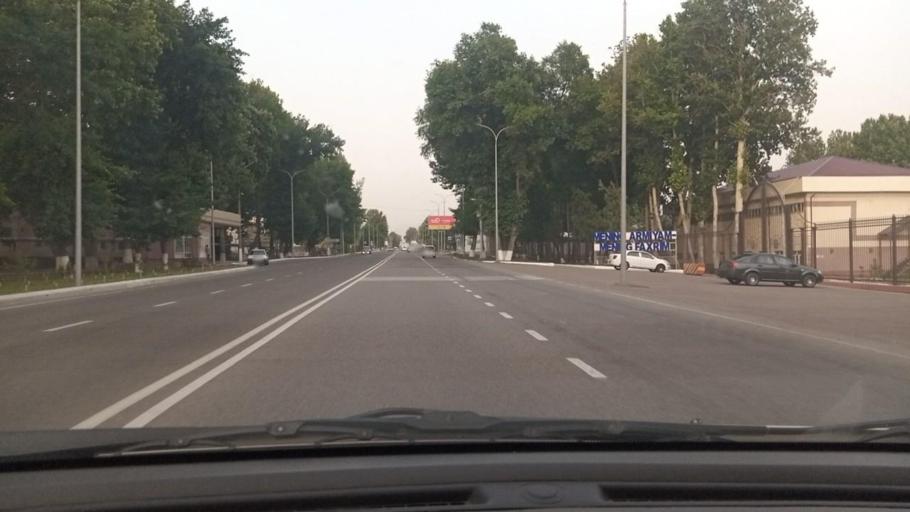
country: UZ
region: Toshkent
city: Angren
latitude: 40.9946
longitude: 70.0572
